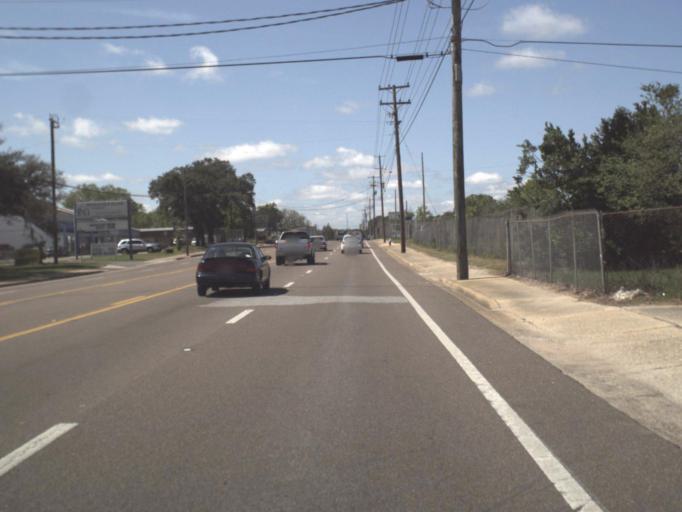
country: US
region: Florida
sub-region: Escambia County
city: Goulding
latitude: 30.4524
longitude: -87.2336
